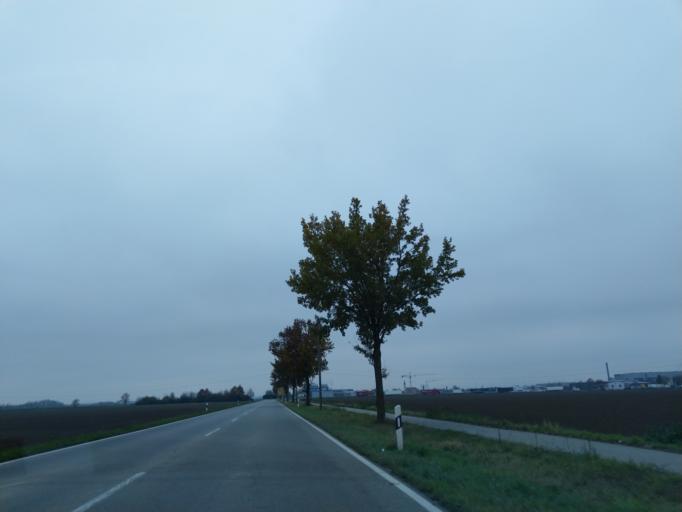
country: DE
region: Bavaria
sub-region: Lower Bavaria
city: Plattling
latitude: 48.7892
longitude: 12.8587
